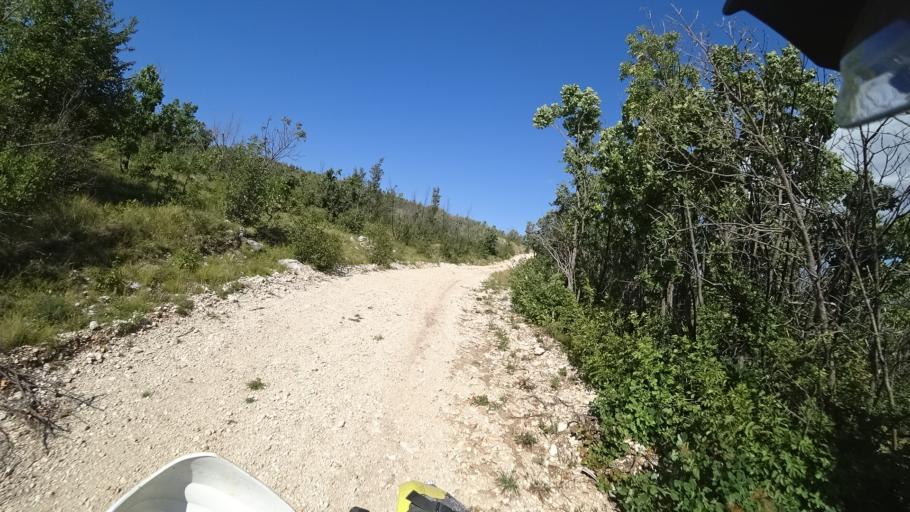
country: HR
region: Sibensko-Kniniska
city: Knin
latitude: 43.9603
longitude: 16.1537
